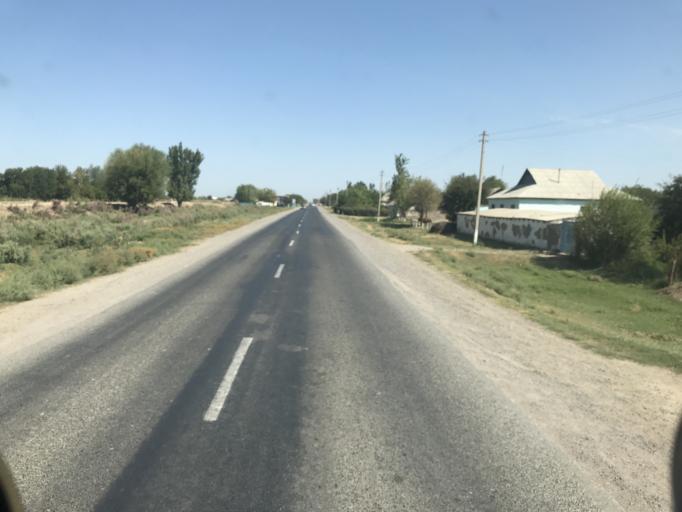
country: KZ
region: Ongtustik Qazaqstan
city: Myrzakent
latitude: 40.7576
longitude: 68.5371
